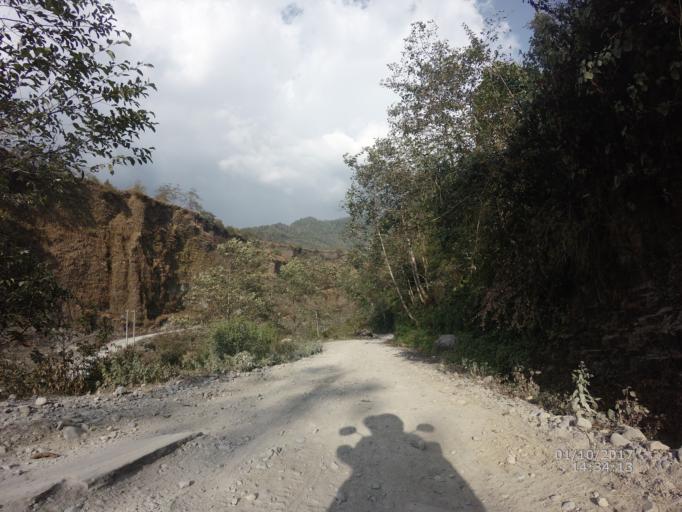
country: NP
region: Western Region
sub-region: Gandaki Zone
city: Pokhara
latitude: 28.3406
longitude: 83.9644
